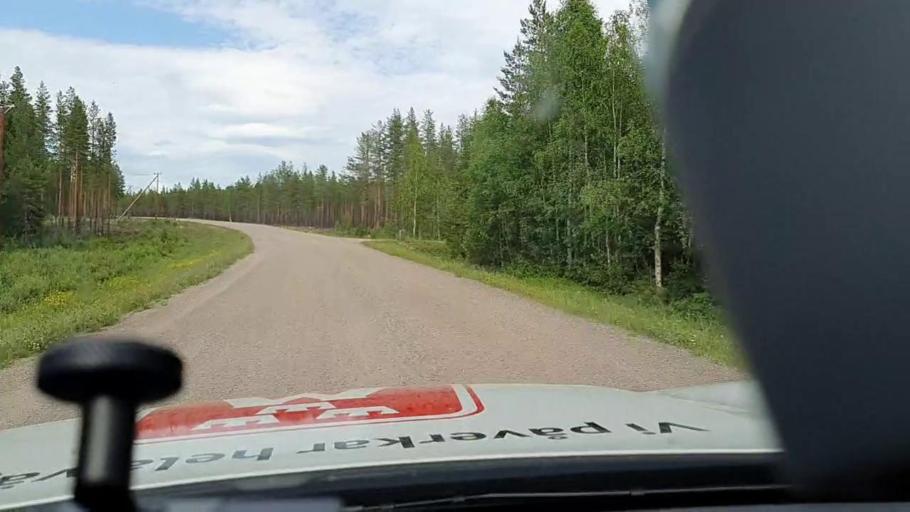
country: SE
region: Norrbotten
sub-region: Alvsbyns Kommun
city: AElvsbyn
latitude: 66.1212
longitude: 20.9898
